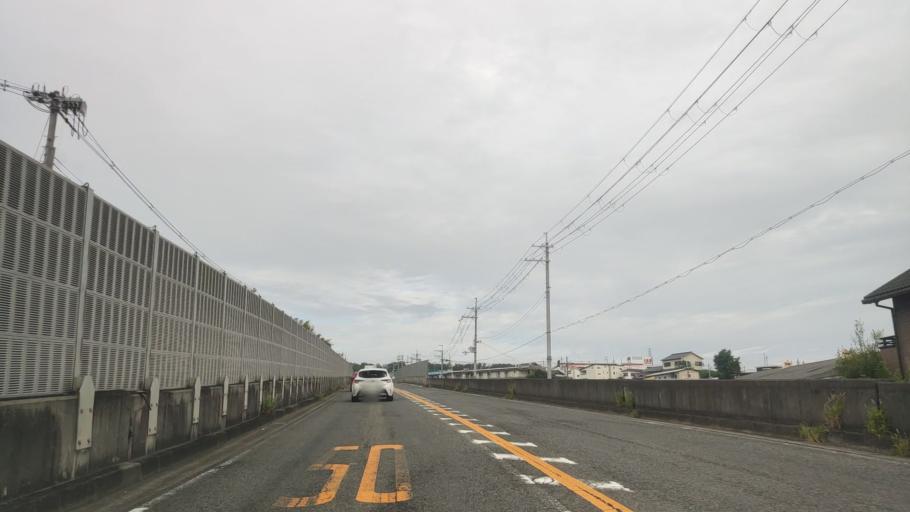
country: JP
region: Osaka
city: Tondabayashicho
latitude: 34.4429
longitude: 135.5576
